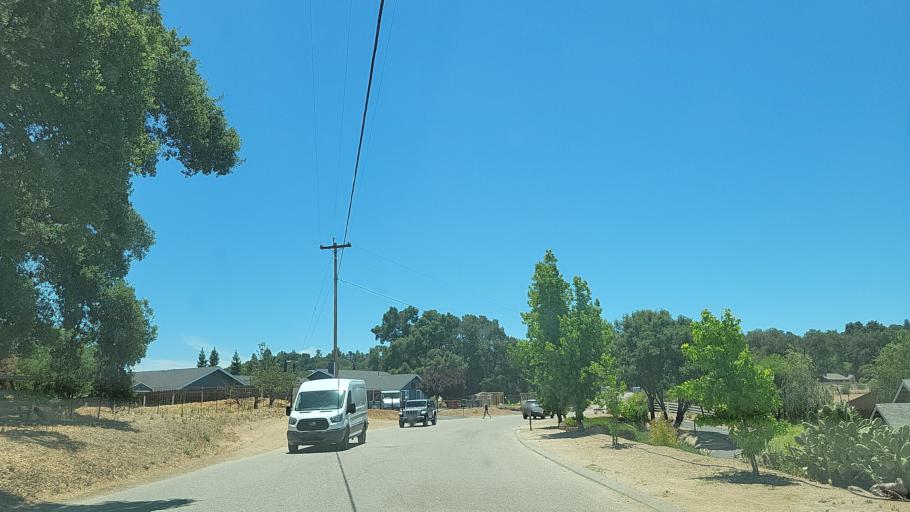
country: US
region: California
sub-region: San Luis Obispo County
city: Atascadero
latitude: 35.5170
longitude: -120.6795
